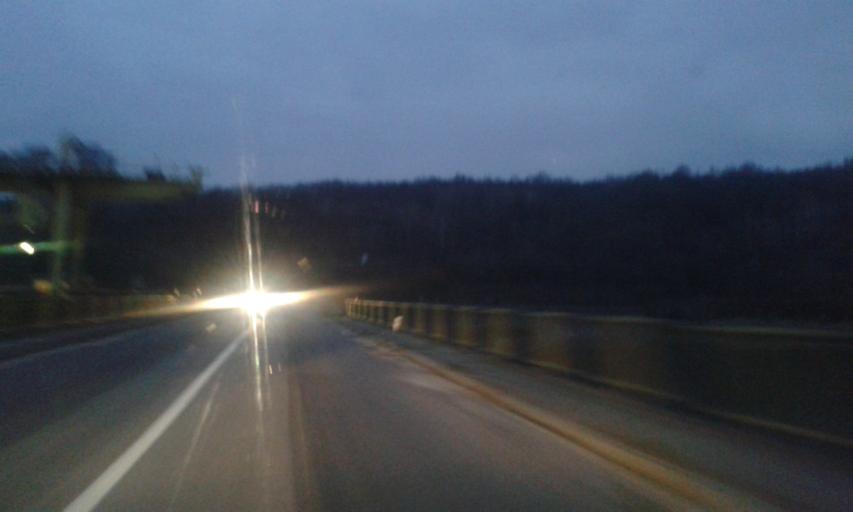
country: RO
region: Gorj
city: Targu Jiu
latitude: 45.0577
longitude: 23.2693
